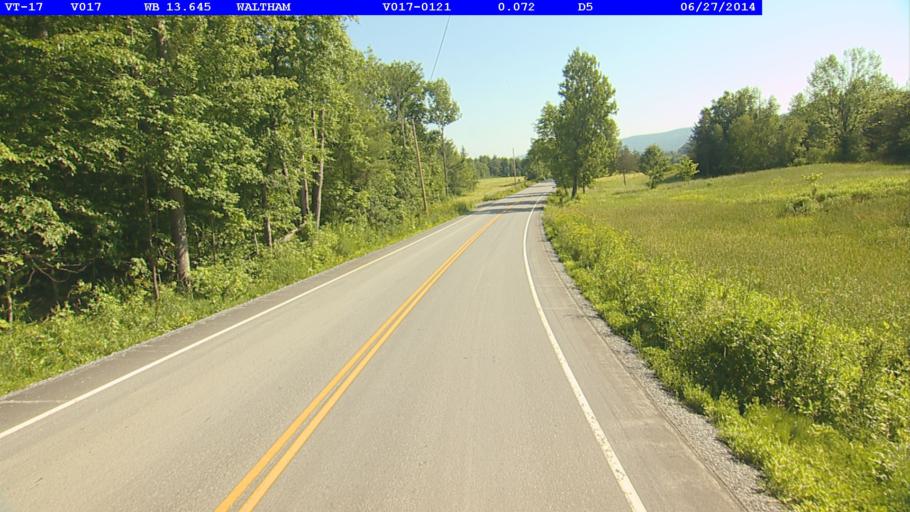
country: US
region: Vermont
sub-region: Addison County
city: Vergennes
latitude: 44.1097
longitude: -73.2182
